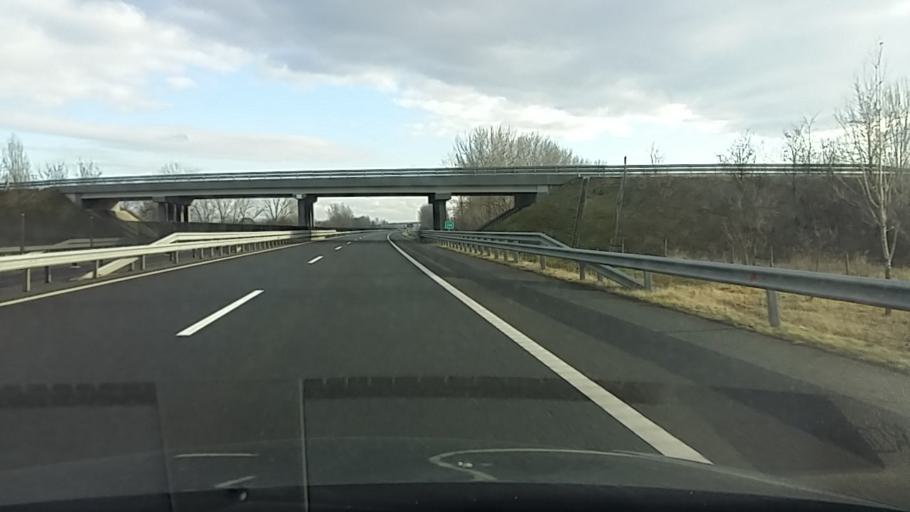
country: HU
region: Szabolcs-Szatmar-Bereg
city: Nyiregyhaza
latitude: 47.8966
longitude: 21.6811
